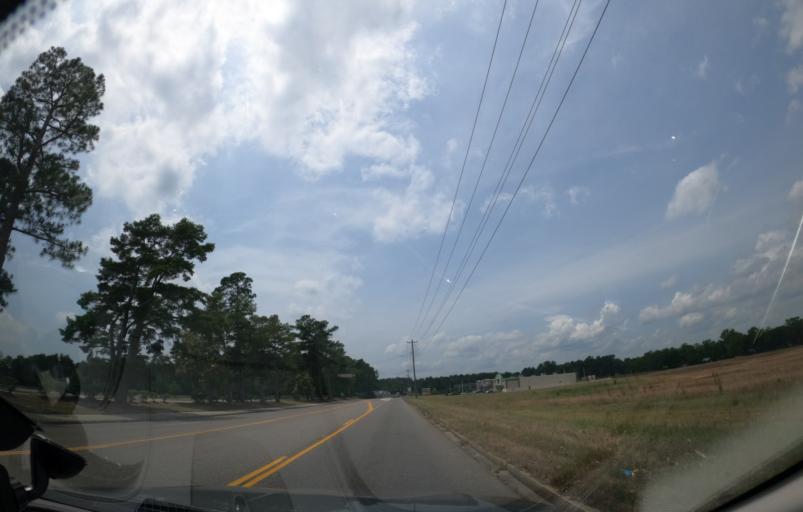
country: US
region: South Carolina
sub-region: Aiken County
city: Aiken
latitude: 33.5800
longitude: -81.7166
